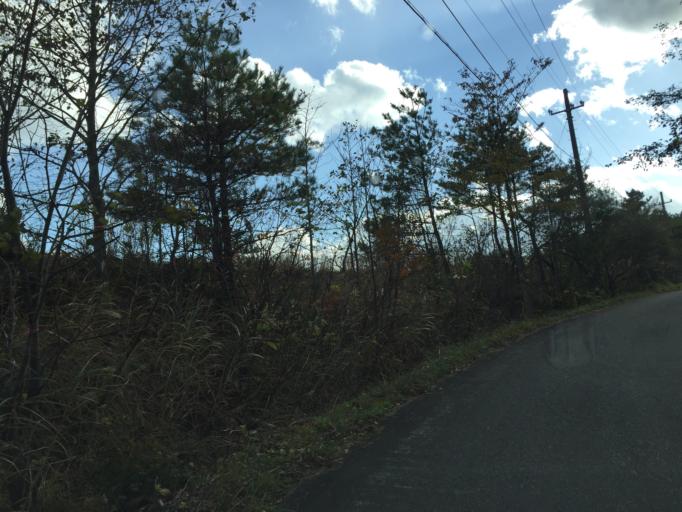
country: JP
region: Fukushima
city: Fukushima-shi
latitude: 37.7331
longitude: 140.3158
